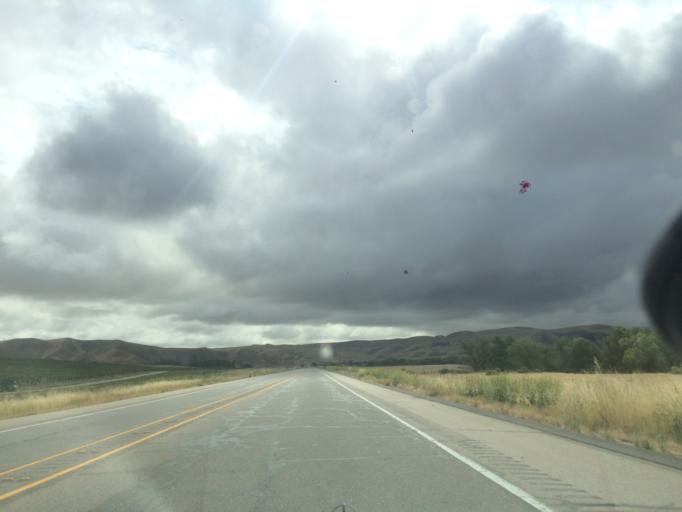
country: US
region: California
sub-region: San Luis Obispo County
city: Shandon
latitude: 35.6625
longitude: -120.3862
